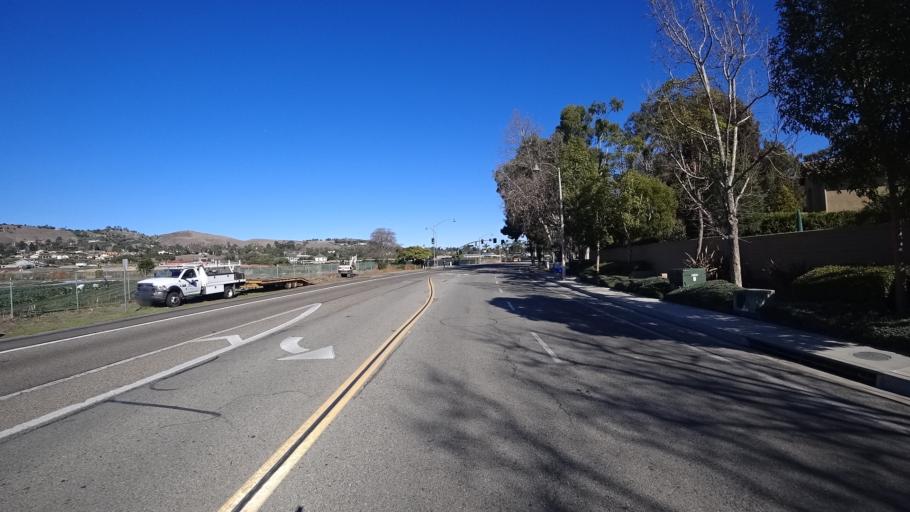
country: US
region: California
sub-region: Orange County
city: San Juan Capistrano
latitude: 33.4898
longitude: -117.6723
